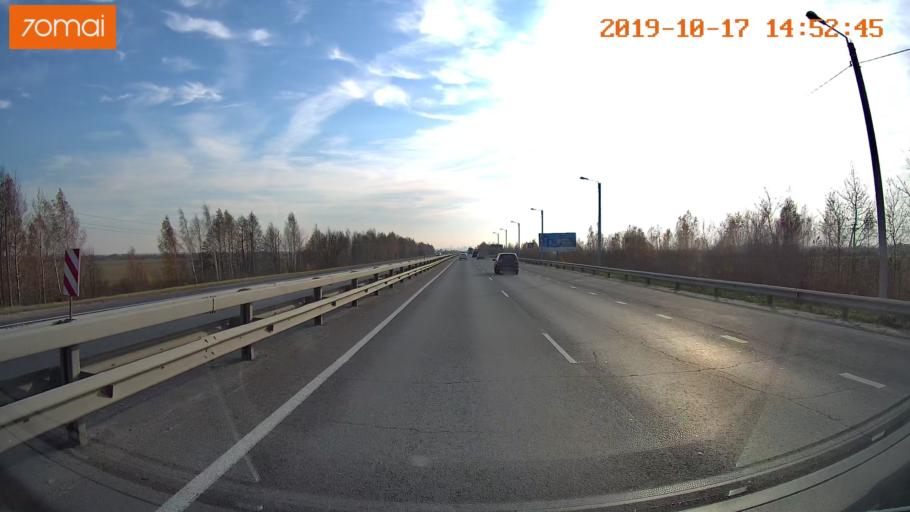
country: RU
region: Rjazan
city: Polyany
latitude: 54.7034
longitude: 39.8435
